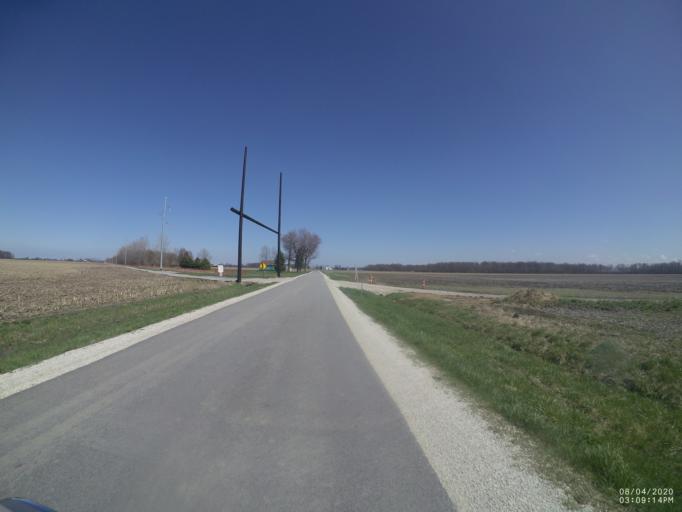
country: US
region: Ohio
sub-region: Sandusky County
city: Stony Prairie
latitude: 41.2823
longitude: -83.2281
